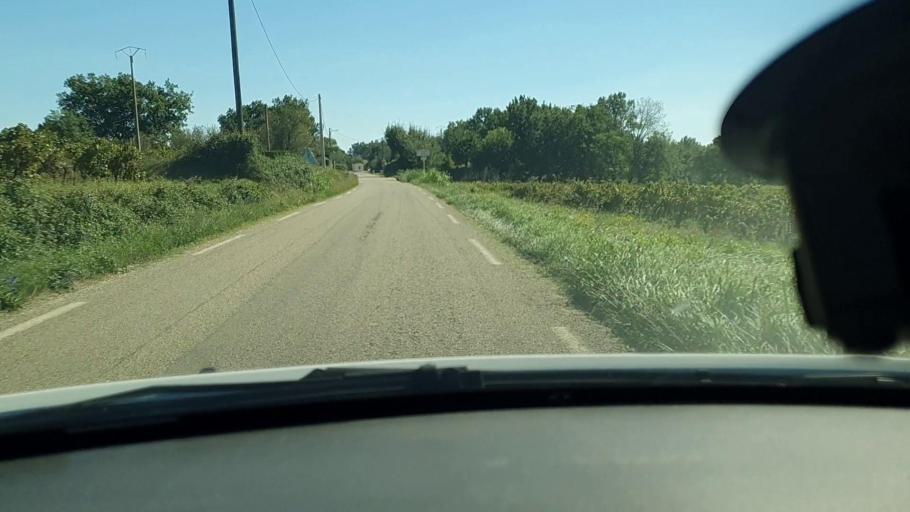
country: FR
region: Languedoc-Roussillon
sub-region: Departement du Gard
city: Goudargues
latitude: 44.2117
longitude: 4.5211
